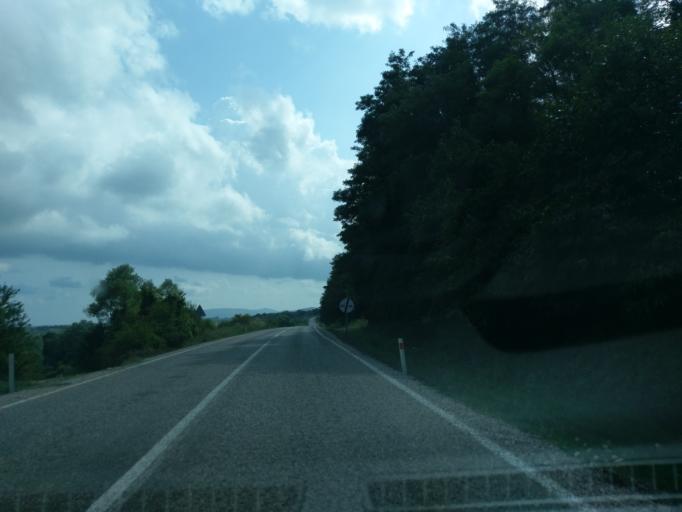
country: TR
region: Sinop
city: Sinop
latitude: 42.0319
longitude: 35.0203
